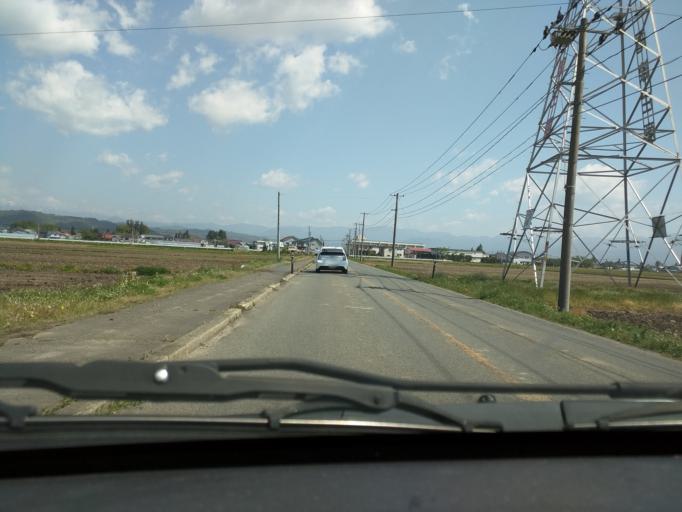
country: JP
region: Fukushima
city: Kitakata
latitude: 37.5832
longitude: 139.8344
